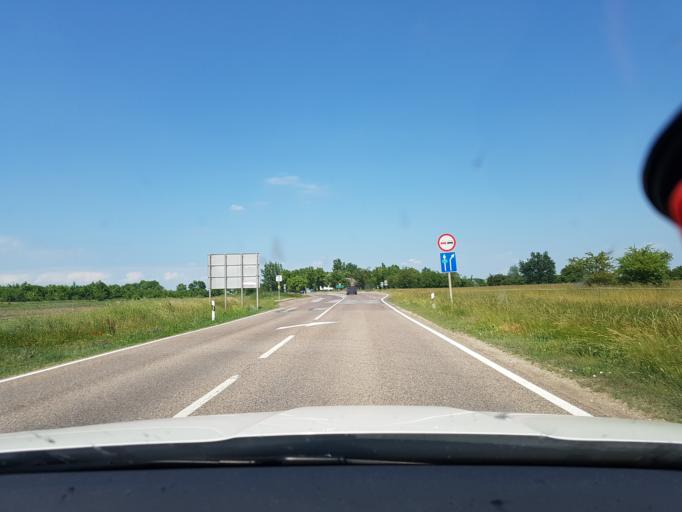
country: HU
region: Hajdu-Bihar
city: Egyek
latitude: 47.5889
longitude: 20.8529
